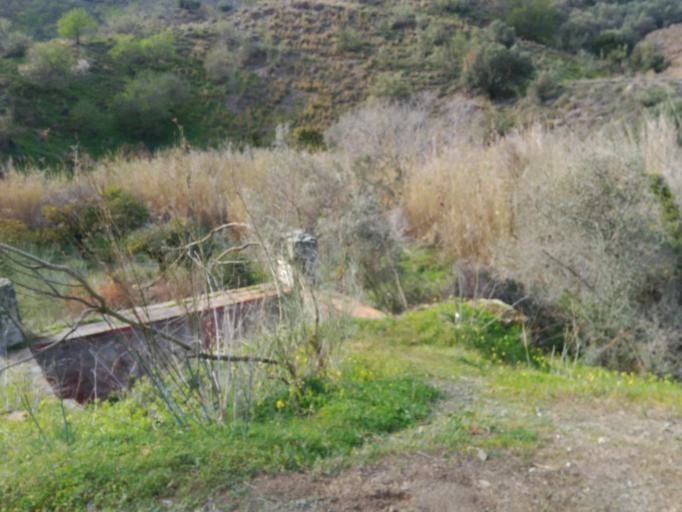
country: ES
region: Andalusia
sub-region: Provincia de Malaga
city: Valdes
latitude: 36.7375
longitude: -4.2243
